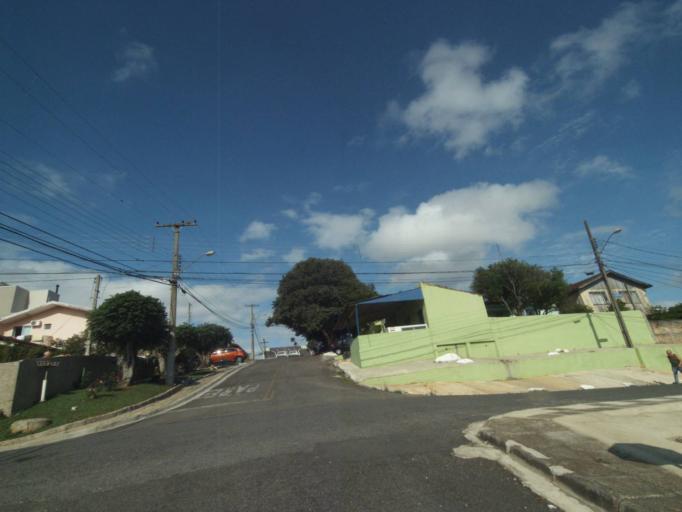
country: BR
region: Parana
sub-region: Curitiba
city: Curitiba
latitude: -25.3905
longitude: -49.3018
